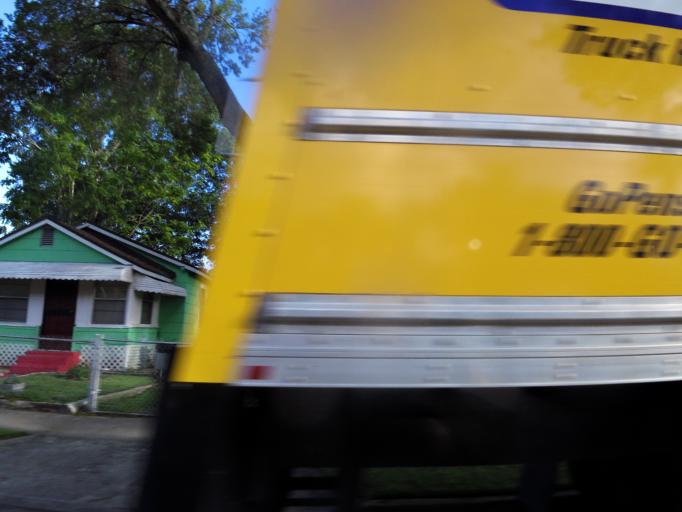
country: US
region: Florida
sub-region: Duval County
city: Jacksonville
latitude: 30.3596
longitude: -81.6713
